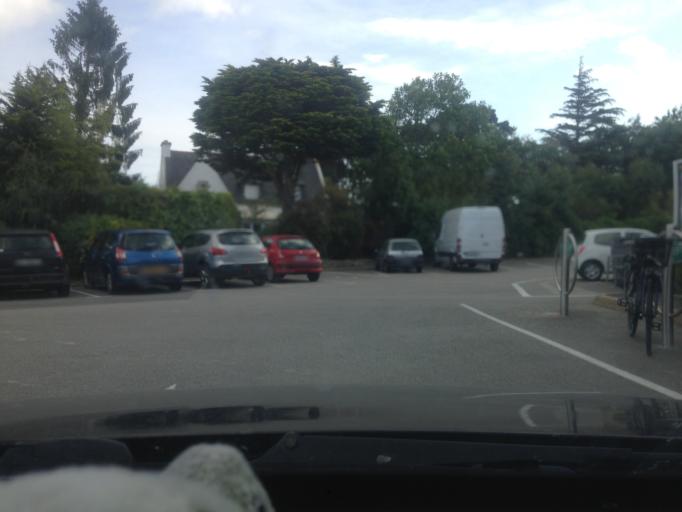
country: FR
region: Brittany
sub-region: Departement du Morbihan
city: Carnac
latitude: 47.5855
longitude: -3.0847
